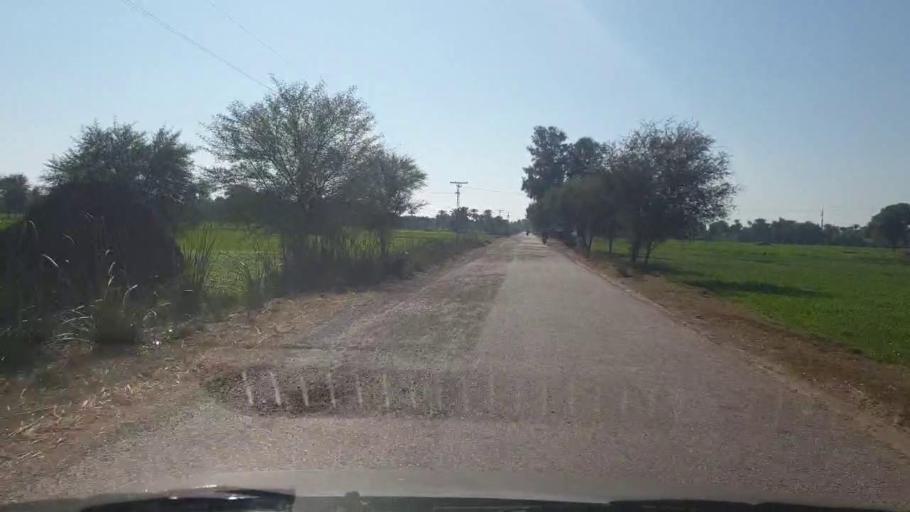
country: PK
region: Sindh
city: Bozdar
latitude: 27.1107
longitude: 68.6339
